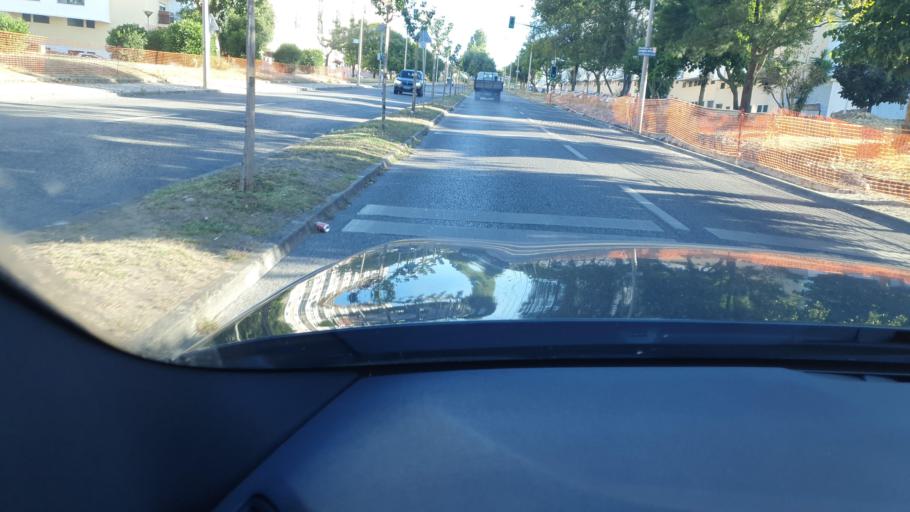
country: PT
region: Lisbon
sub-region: Sintra
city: Cacem
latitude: 38.7632
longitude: -9.2787
